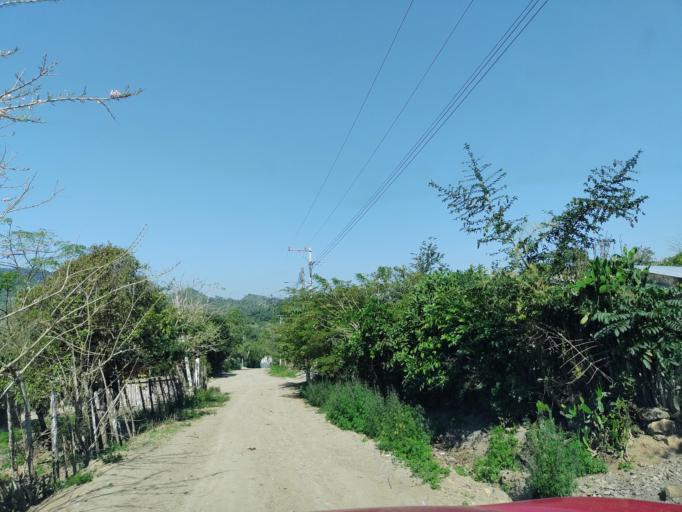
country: MX
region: Veracruz
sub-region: Papantla
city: Polutla
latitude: 20.5179
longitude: -97.2432
